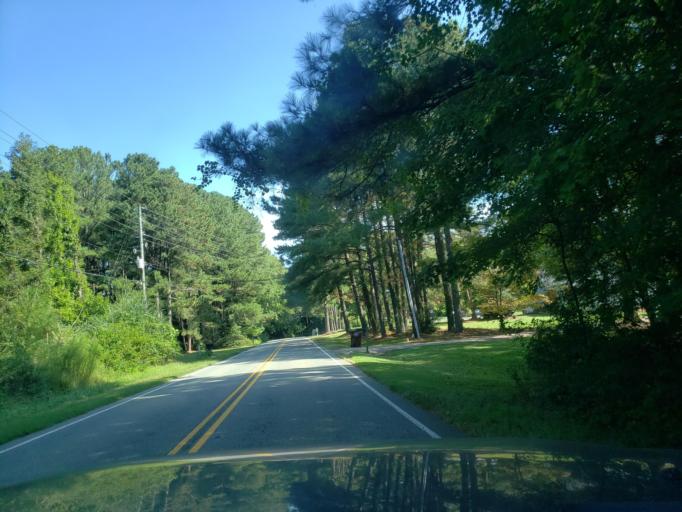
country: US
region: North Carolina
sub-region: Wake County
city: West Raleigh
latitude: 35.9368
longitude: -78.7028
